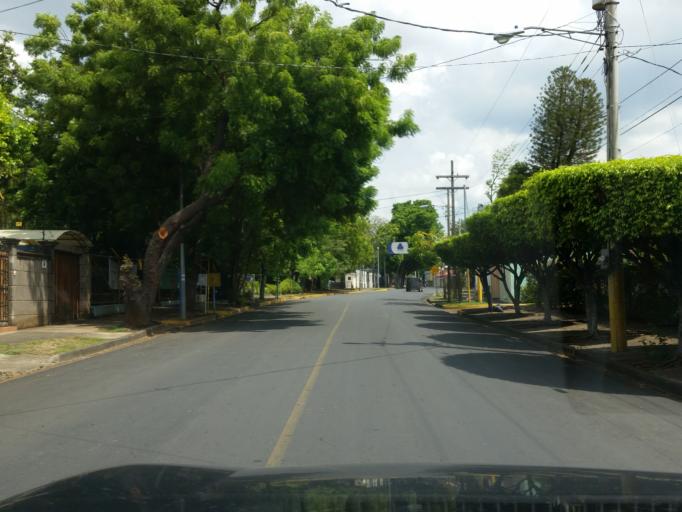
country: NI
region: Managua
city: Ciudad Sandino
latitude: 12.1417
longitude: -86.2994
